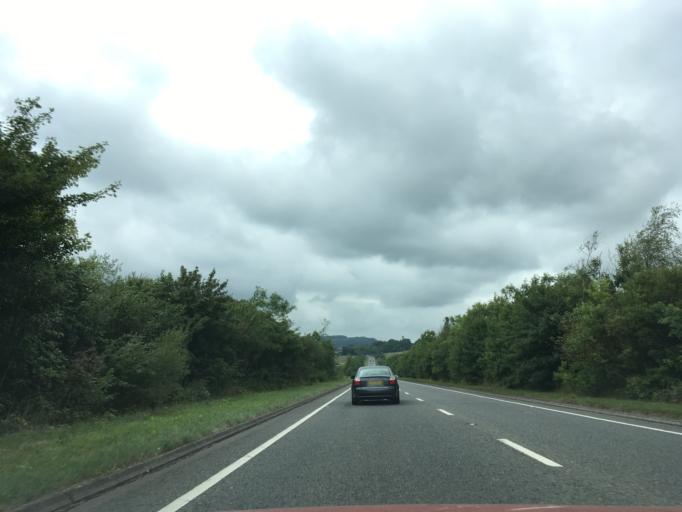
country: GB
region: Wales
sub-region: Carmarthenshire
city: Whitland
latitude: 51.8254
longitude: -4.6007
